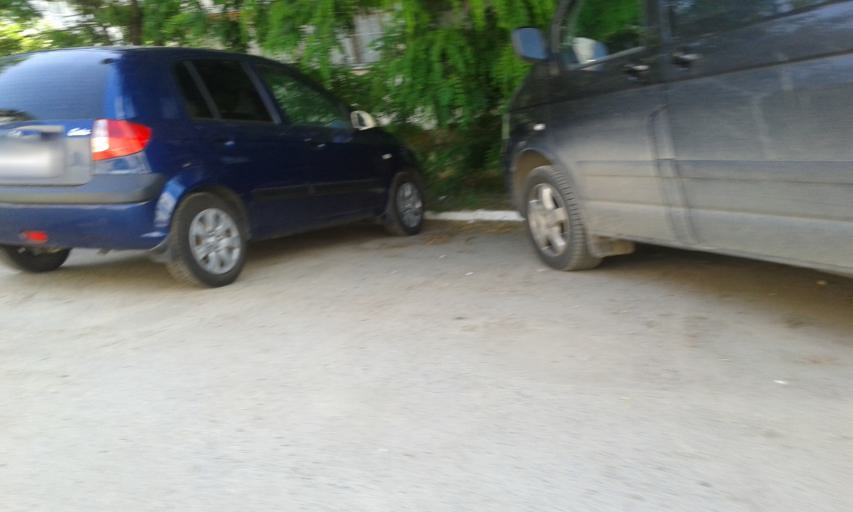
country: RU
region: Volgograd
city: Volgograd
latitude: 48.7555
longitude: 44.5105
